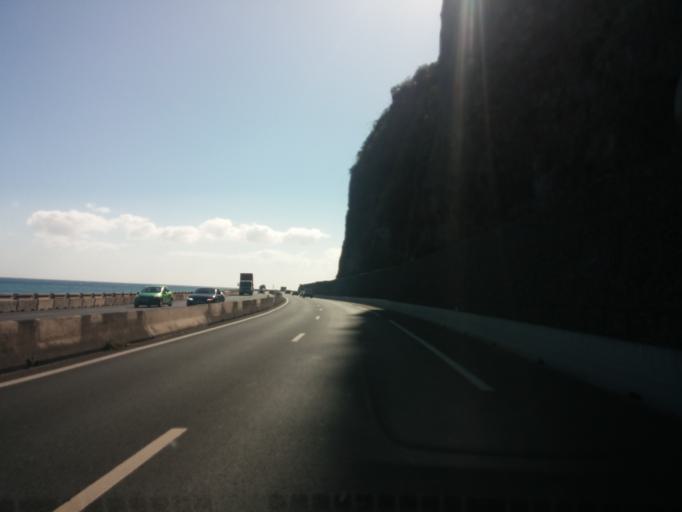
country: RE
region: Reunion
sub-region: Reunion
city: La Possession
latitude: -20.9183
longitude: 55.3490
